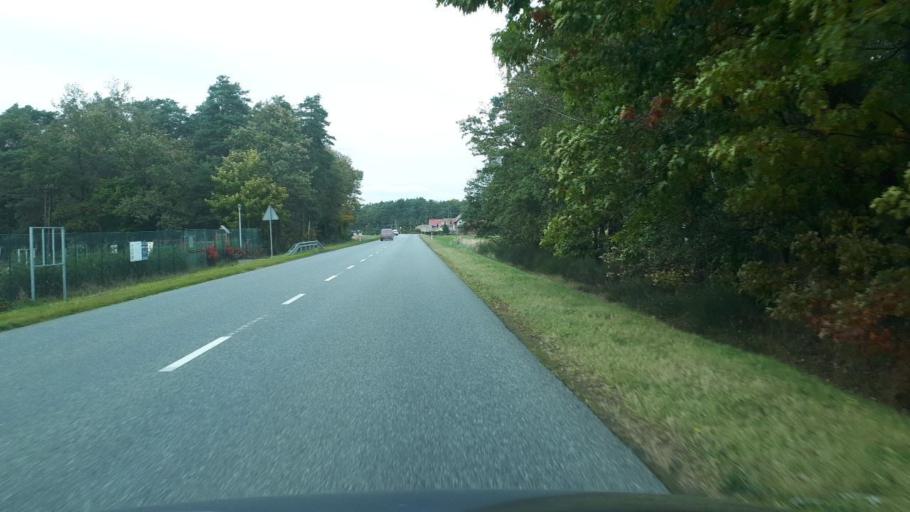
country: PL
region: Opole Voivodeship
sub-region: Powiat oleski
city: Dobrodzien
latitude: 50.7726
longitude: 18.4295
